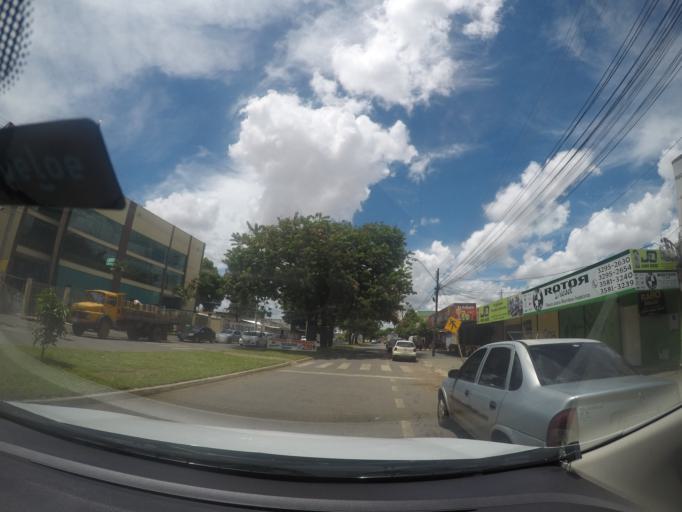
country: BR
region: Goias
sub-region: Goiania
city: Goiania
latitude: -16.6773
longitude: -49.3106
